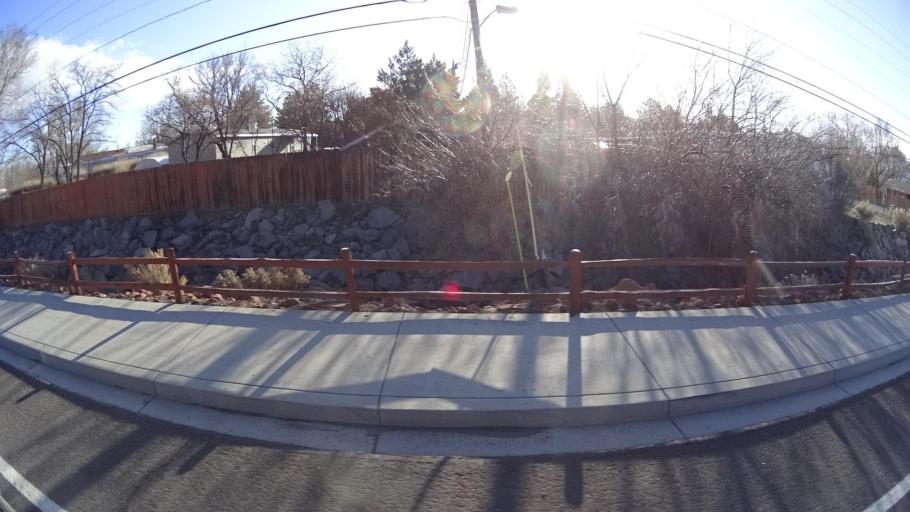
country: US
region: Nevada
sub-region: Washoe County
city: Cold Springs
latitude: 39.6794
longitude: -119.9787
